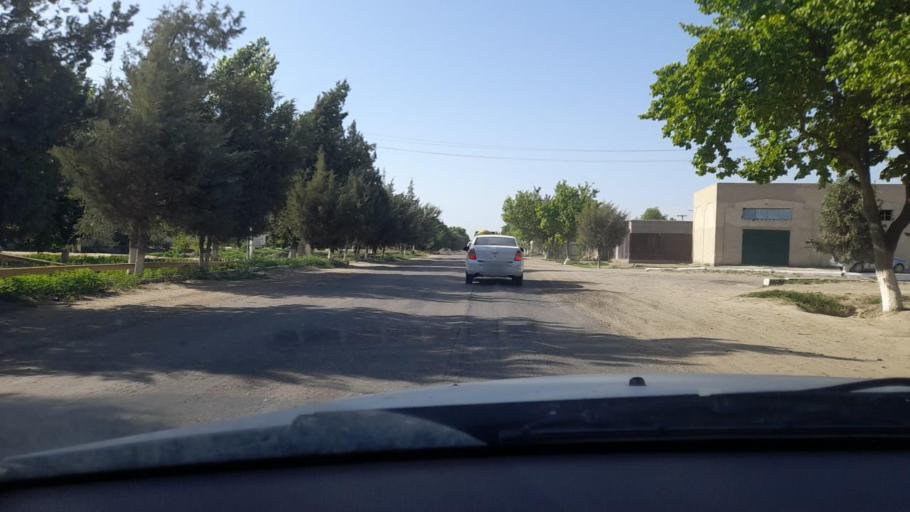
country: UZ
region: Bukhara
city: Romiton
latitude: 40.0618
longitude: 64.3274
